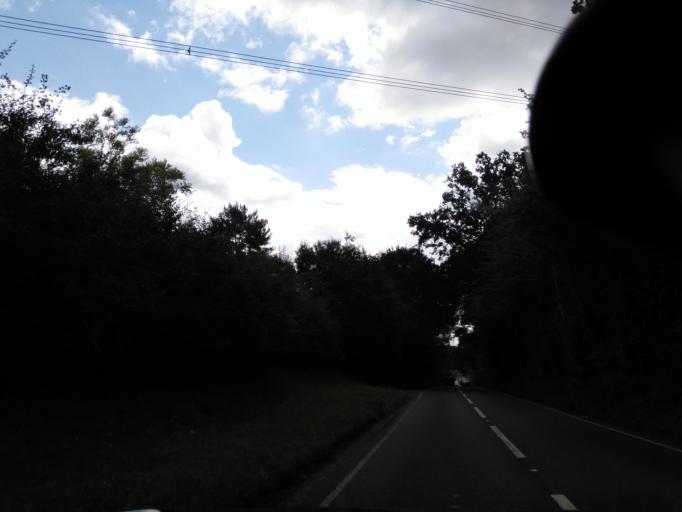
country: GB
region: England
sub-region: Dorset
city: Lytchett Matravers
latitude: 50.7805
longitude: -2.0720
